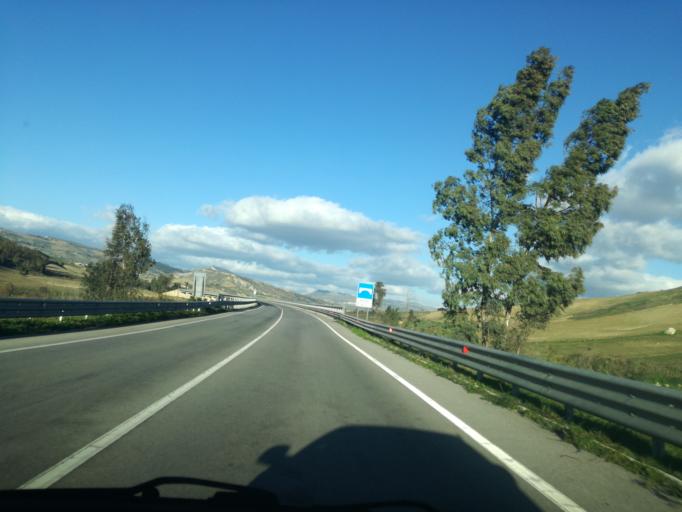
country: IT
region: Sicily
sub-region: Enna
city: Pietraperzia
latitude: 37.4387
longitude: 14.0960
